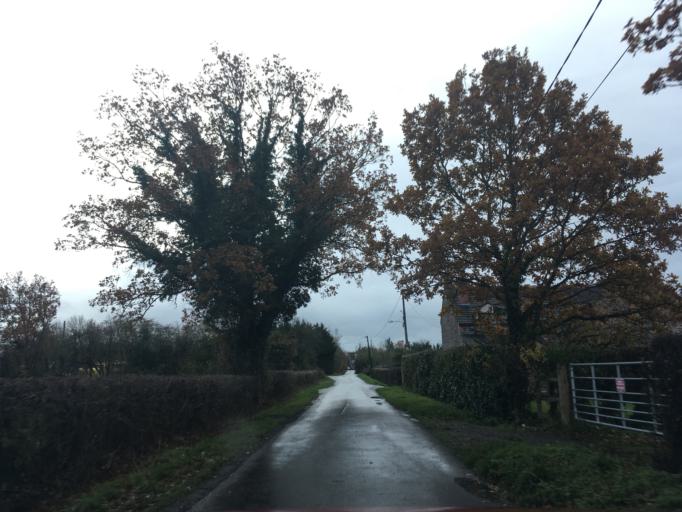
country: GB
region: England
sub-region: South Gloucestershire
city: Yate
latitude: 51.5530
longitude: -2.4330
